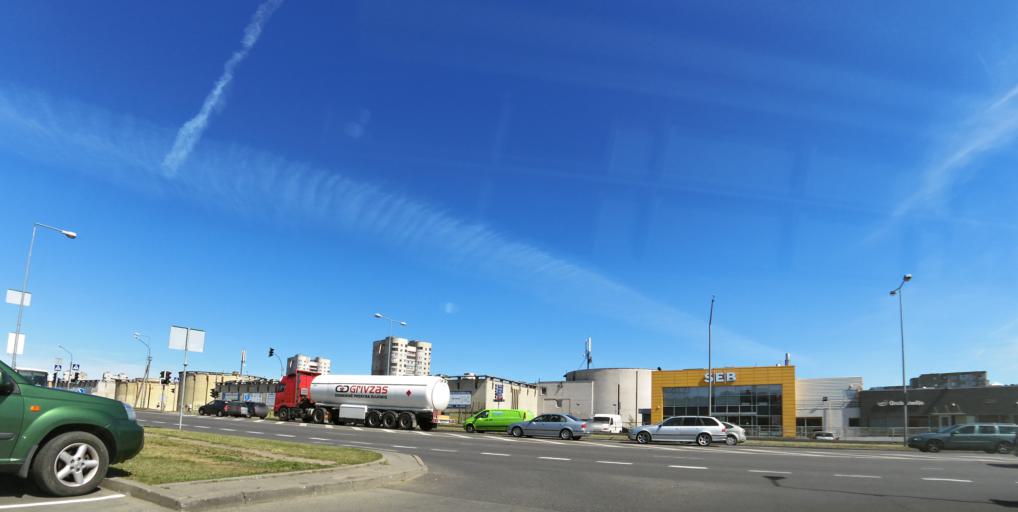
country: LT
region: Vilnius County
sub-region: Vilnius
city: Fabijoniskes
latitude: 54.7222
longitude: 25.2432
